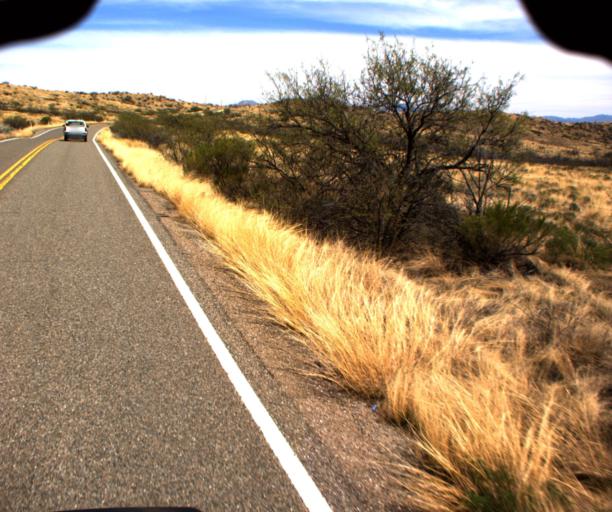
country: US
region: Arizona
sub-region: Cochise County
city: Willcox
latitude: 32.1673
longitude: -109.5862
